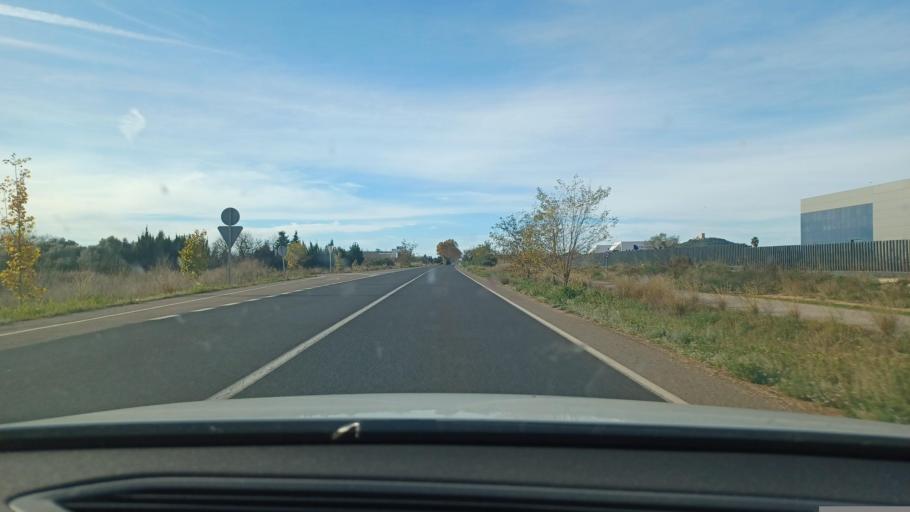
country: ES
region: Catalonia
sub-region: Provincia de Tarragona
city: Ulldecona
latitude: 40.6087
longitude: 0.4603
